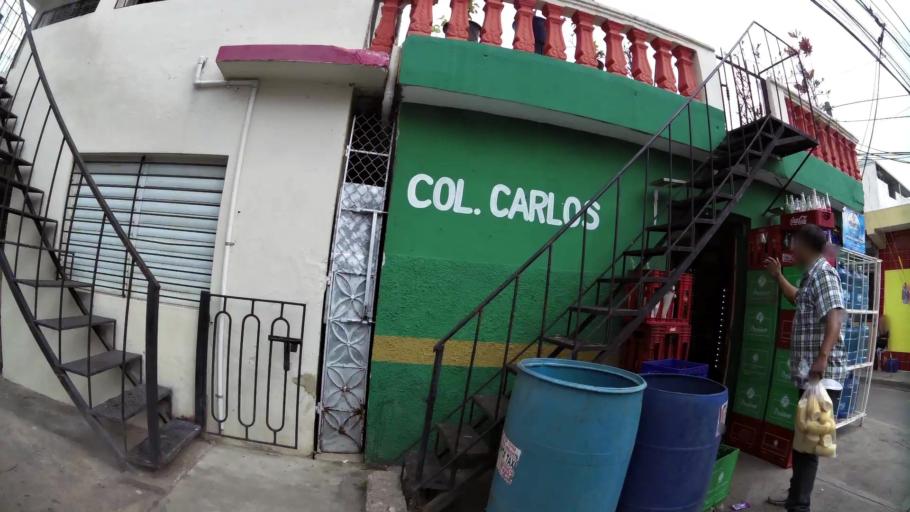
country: DO
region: Santiago
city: Santiago de los Caballeros
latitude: 19.4632
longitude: -70.6690
